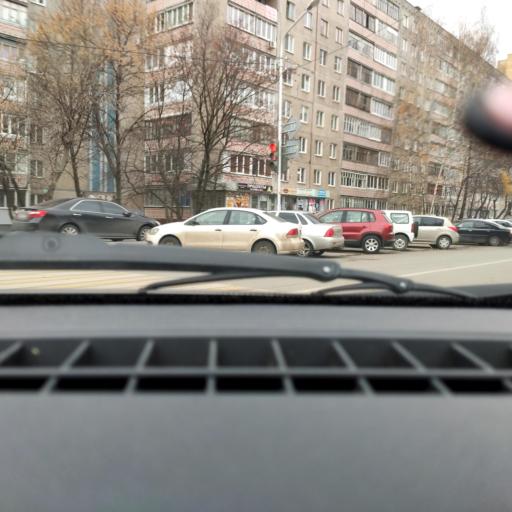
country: RU
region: Bashkortostan
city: Ufa
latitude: 54.7076
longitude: 56.0087
